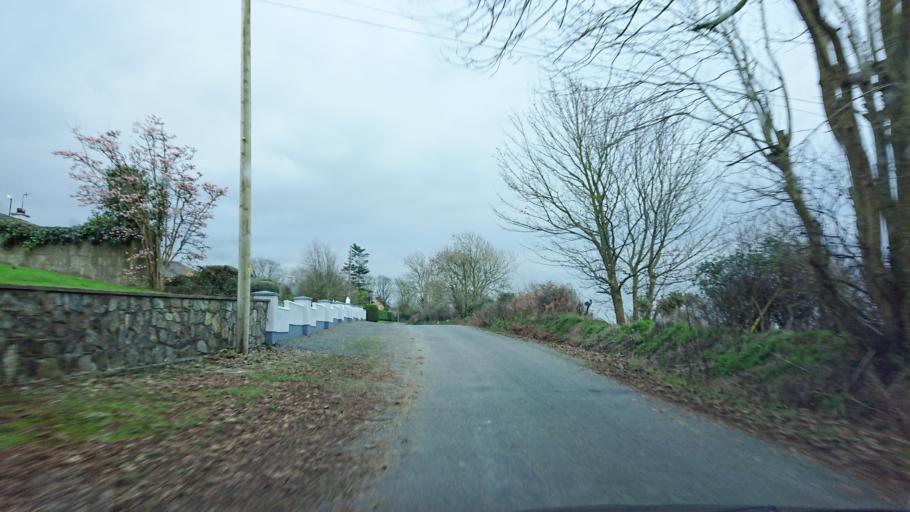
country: IE
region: Munster
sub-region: Waterford
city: Waterford
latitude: 52.2519
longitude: -7.0107
